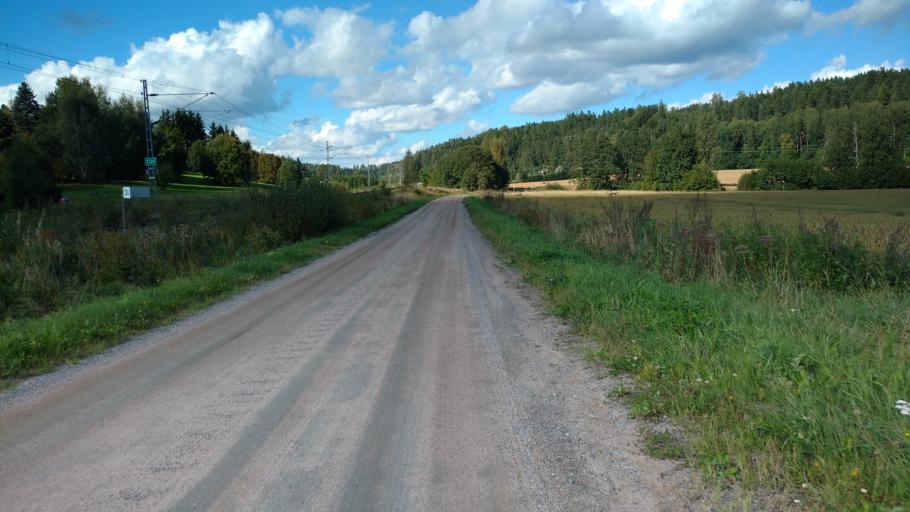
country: FI
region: Varsinais-Suomi
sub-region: Salo
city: Salo
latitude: 60.3081
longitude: 23.1074
